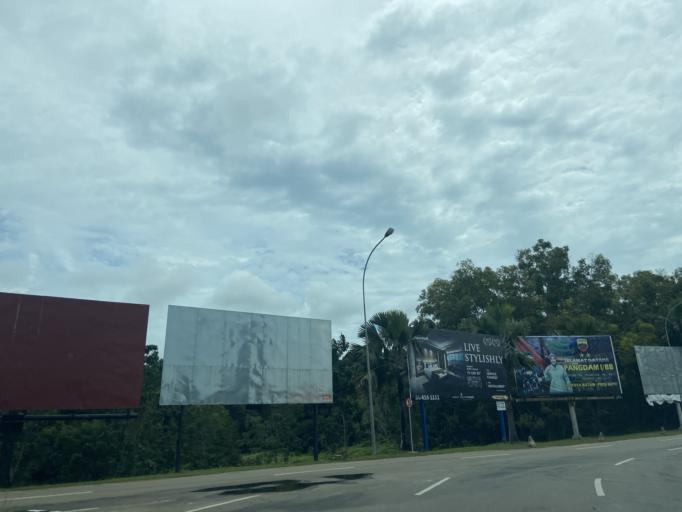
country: SG
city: Singapore
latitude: 1.1229
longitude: 104.1122
